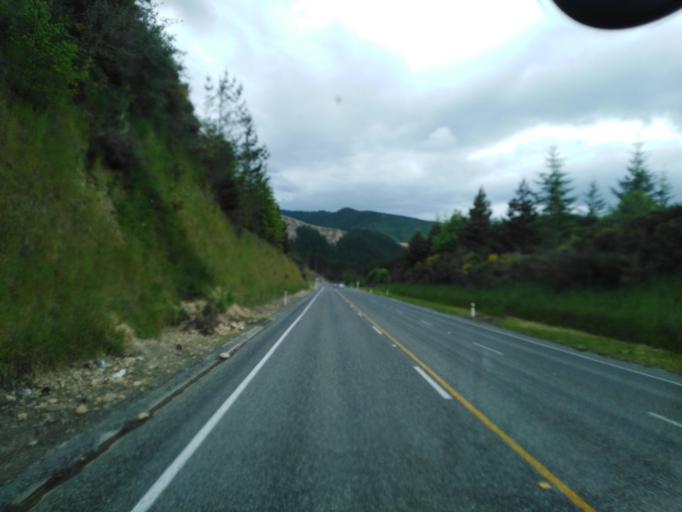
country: NZ
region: Tasman
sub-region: Tasman District
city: Wakefield
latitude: -41.4848
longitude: 172.9040
